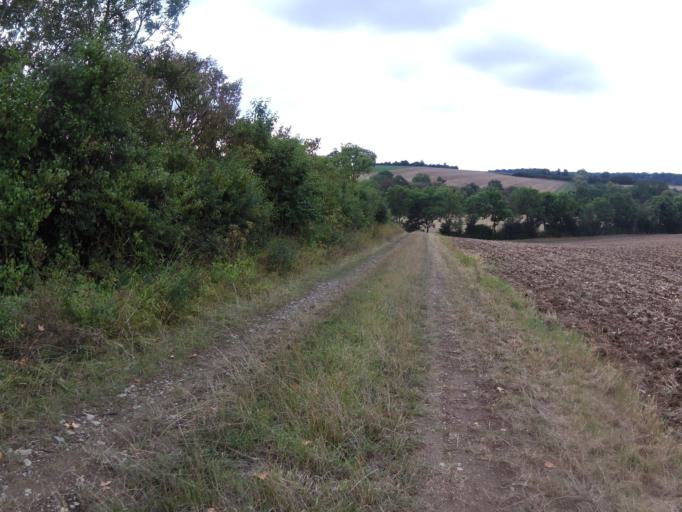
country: DE
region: Bavaria
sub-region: Regierungsbezirk Unterfranken
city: Gadheim
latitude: 49.8517
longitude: 9.9125
